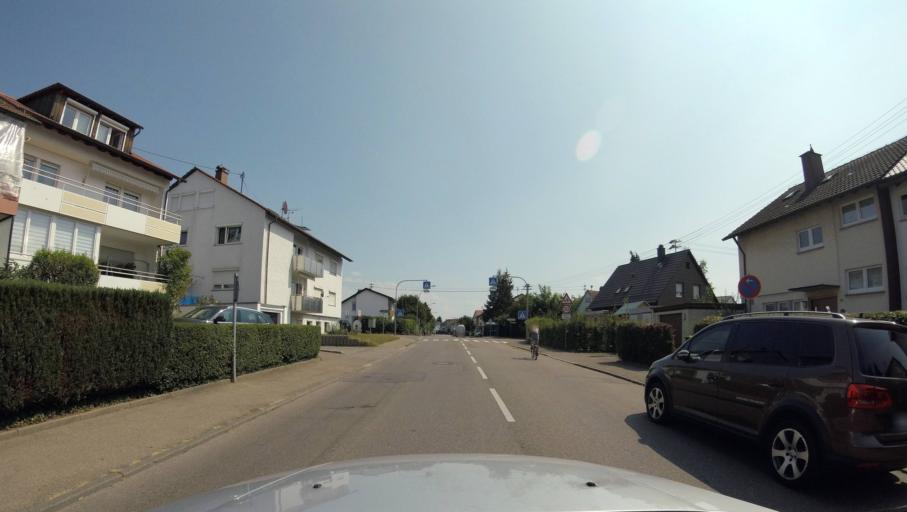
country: DE
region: Baden-Wuerttemberg
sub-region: Regierungsbezirk Stuttgart
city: Backnang
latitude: 48.9533
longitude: 9.4408
